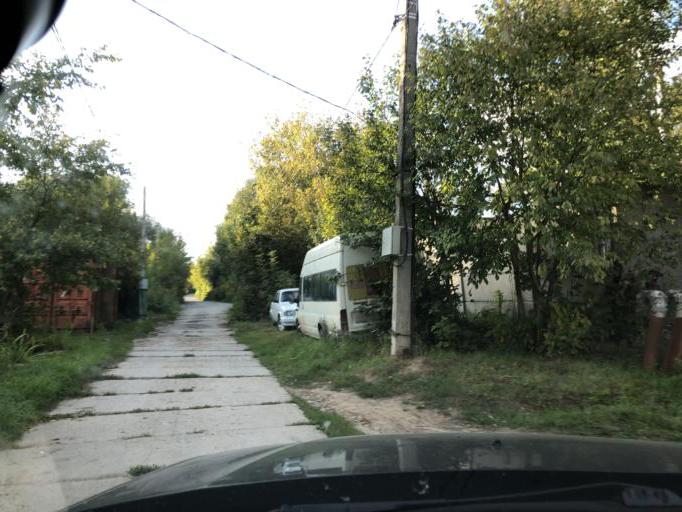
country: RU
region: Tula
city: Mendeleyevskiy
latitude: 54.1829
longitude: 37.5437
